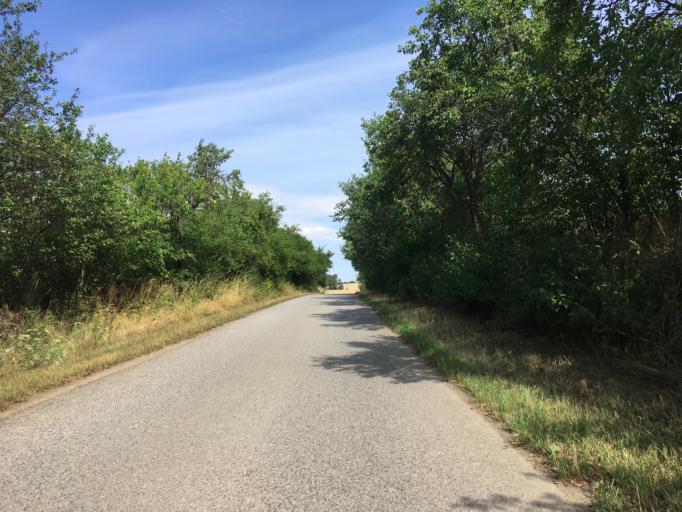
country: DE
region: Brandenburg
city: Casekow
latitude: 53.2127
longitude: 14.1487
